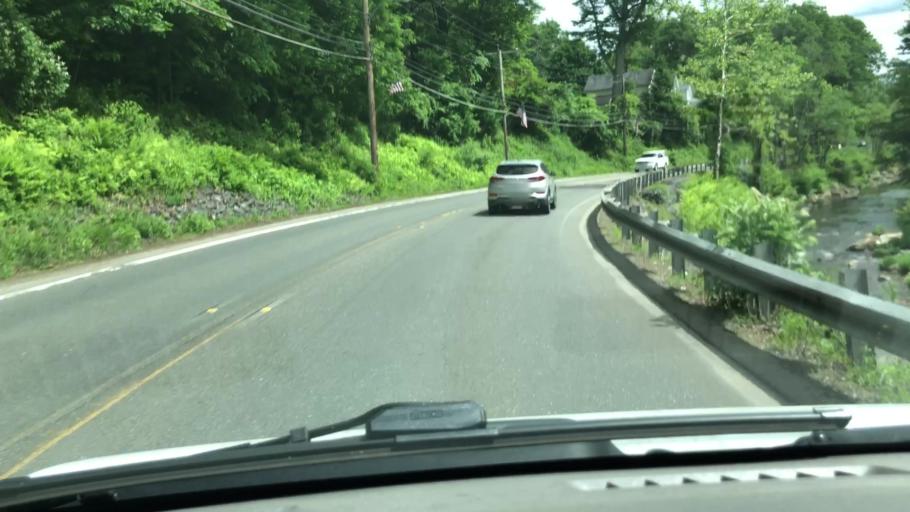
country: US
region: Massachusetts
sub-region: Hampshire County
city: Williamsburg
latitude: 42.3804
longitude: -72.7071
